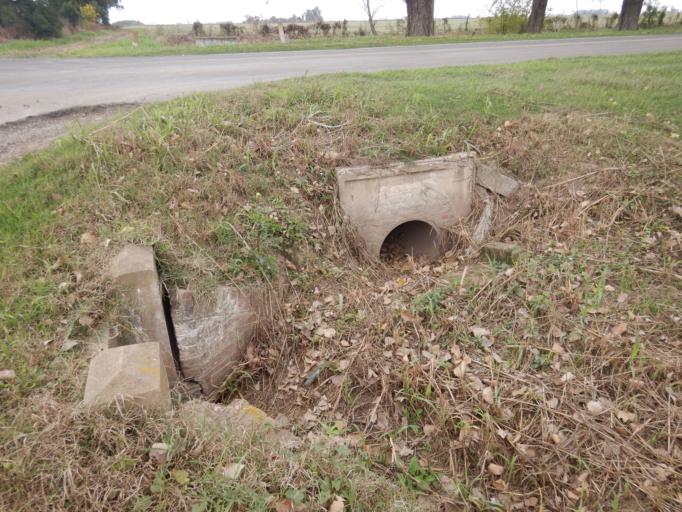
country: AR
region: Santa Fe
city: Carcarana
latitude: -32.8730
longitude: -61.0907
